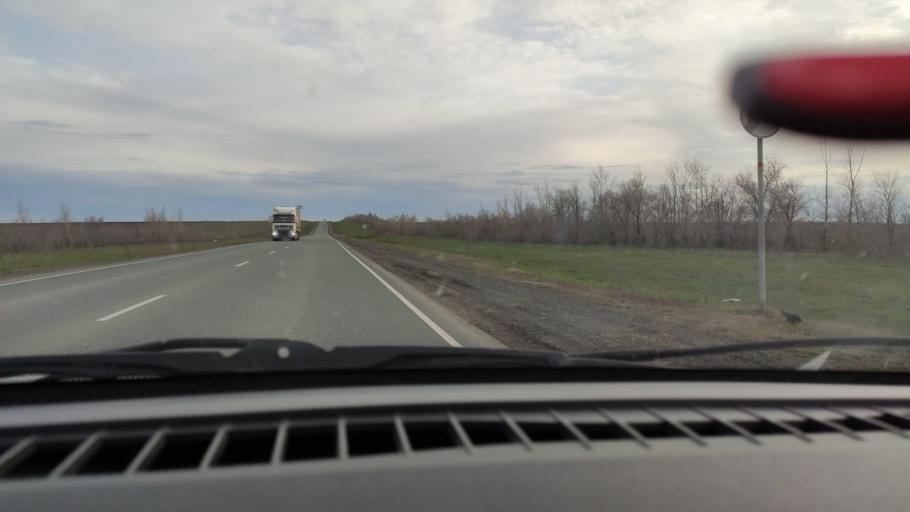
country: RU
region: Orenburg
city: Sakmara
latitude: 52.0787
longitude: 55.2655
